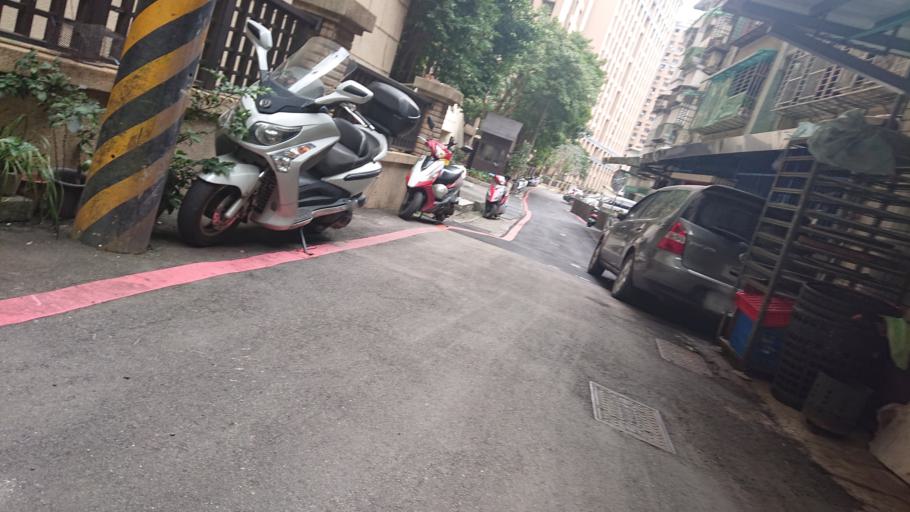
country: TW
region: Taiwan
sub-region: Taoyuan
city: Taoyuan
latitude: 24.9361
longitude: 121.3611
